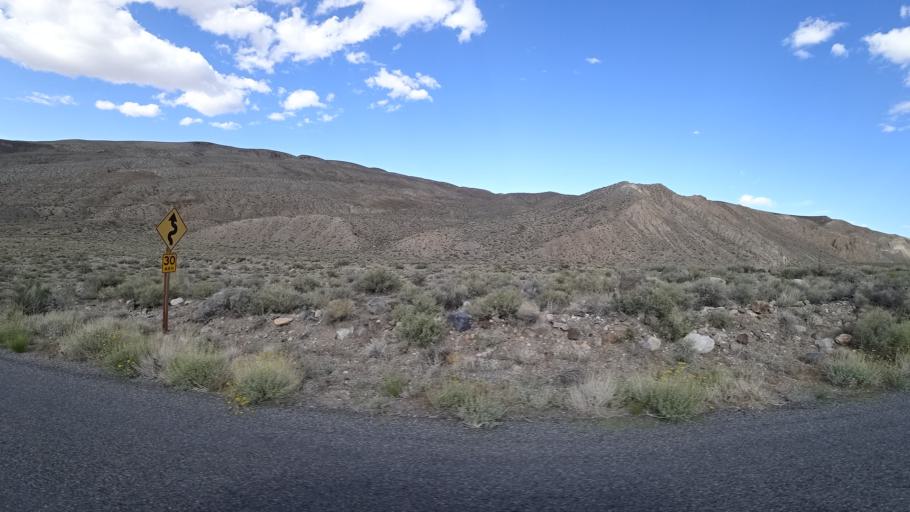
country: US
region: Nevada
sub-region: Nye County
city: Beatty
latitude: 36.4119
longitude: -117.1768
